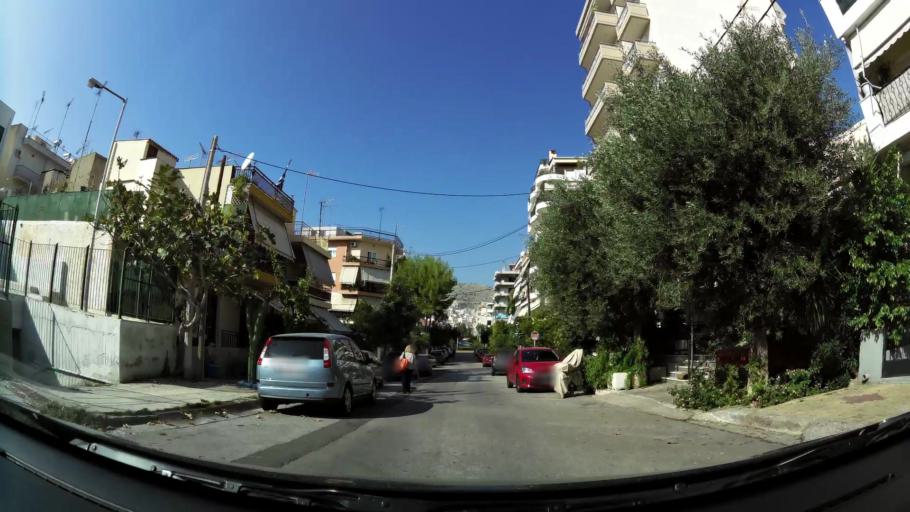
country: GR
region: Attica
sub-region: Nomos Piraios
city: Keratsini
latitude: 37.9635
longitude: 23.6228
